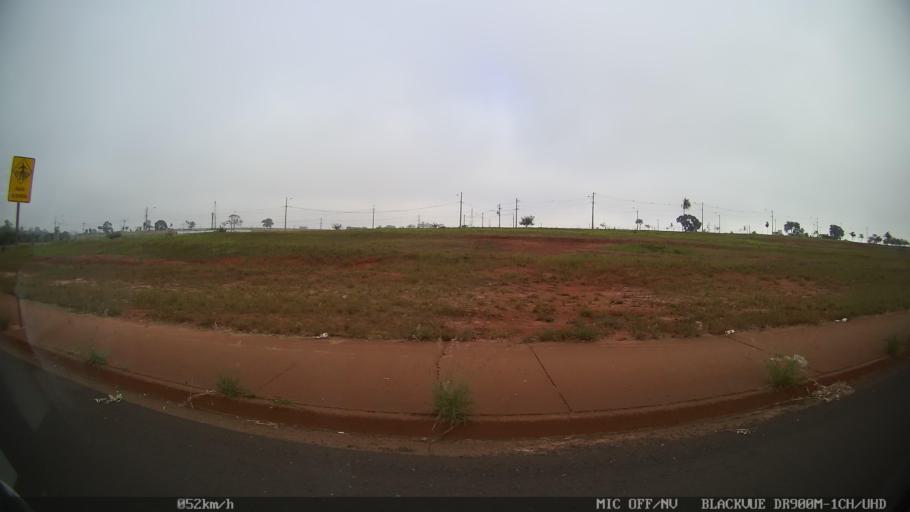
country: BR
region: Sao Paulo
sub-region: Sao Jose Do Rio Preto
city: Sao Jose do Rio Preto
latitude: -20.8574
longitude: -49.3736
